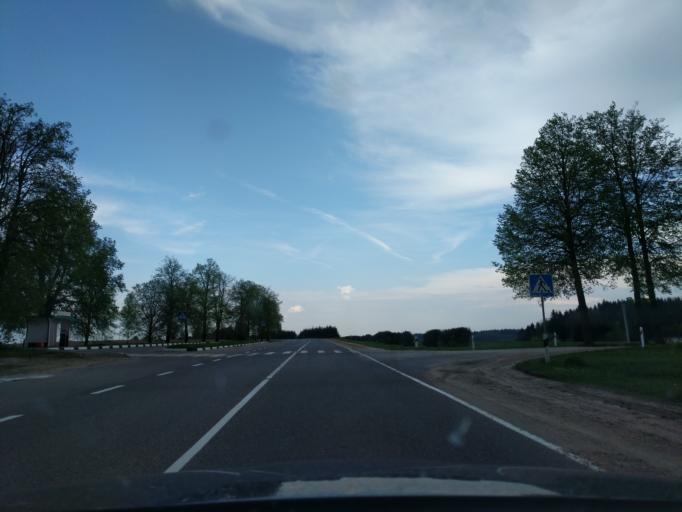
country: BY
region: Grodnenskaya
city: Navahrudak
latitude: 53.6072
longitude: 25.8519
